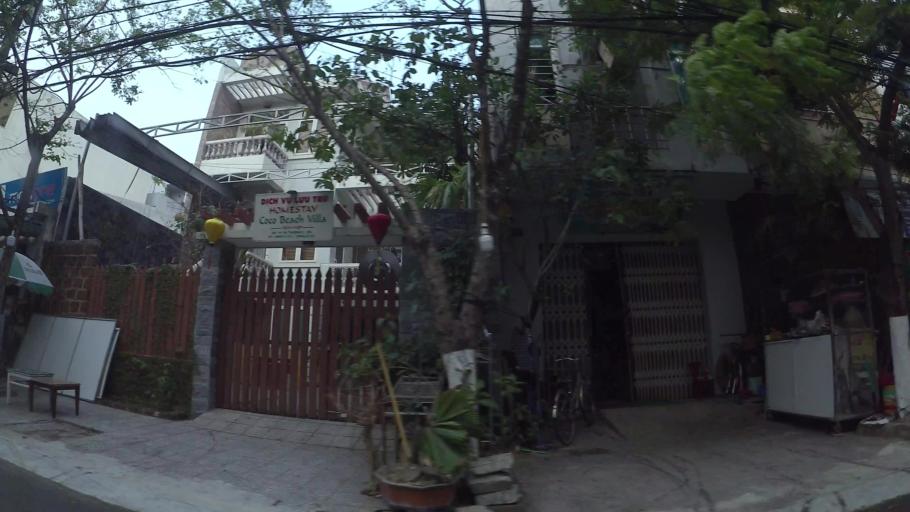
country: VN
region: Da Nang
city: Son Tra
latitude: 16.0485
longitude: 108.2452
